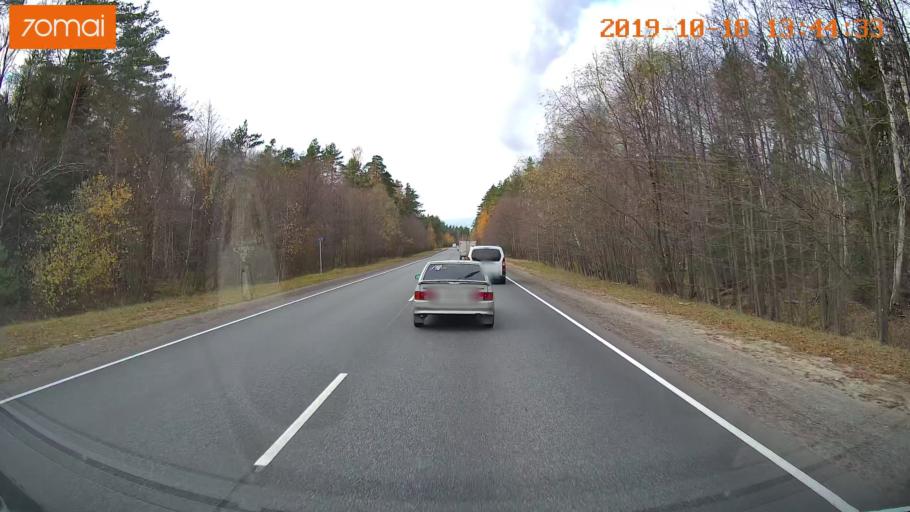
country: RU
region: Rjazan
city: Solotcha
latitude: 54.9378
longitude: 39.9602
